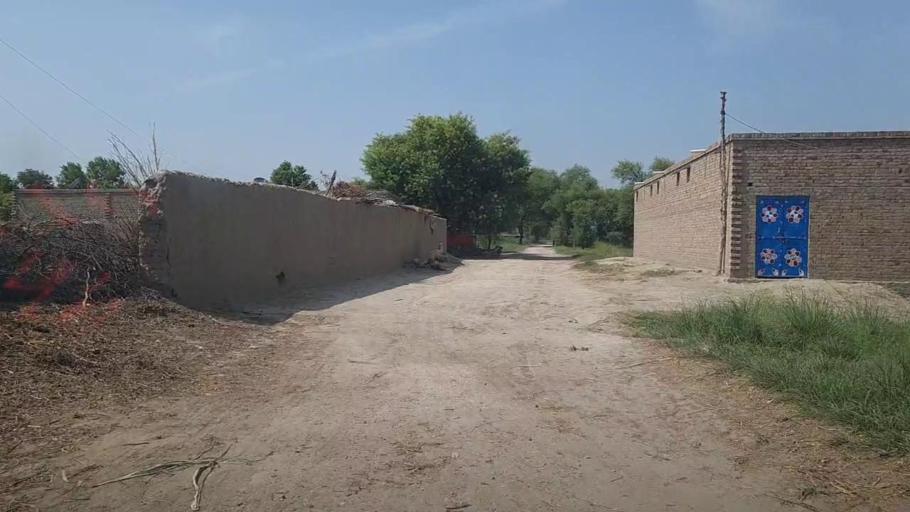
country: PK
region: Sindh
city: Ubauro
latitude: 28.1699
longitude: 69.8161
